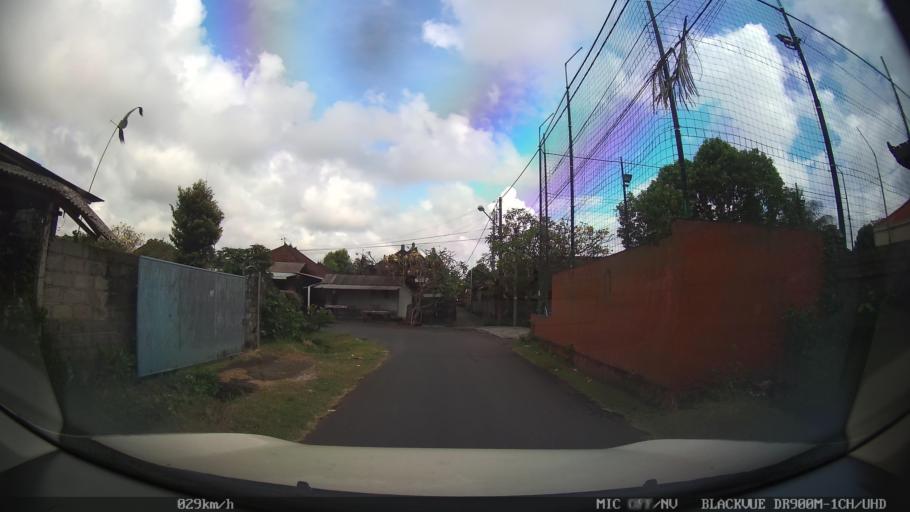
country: ID
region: Bali
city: Banjar Bucu
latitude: -8.5905
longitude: 115.2072
